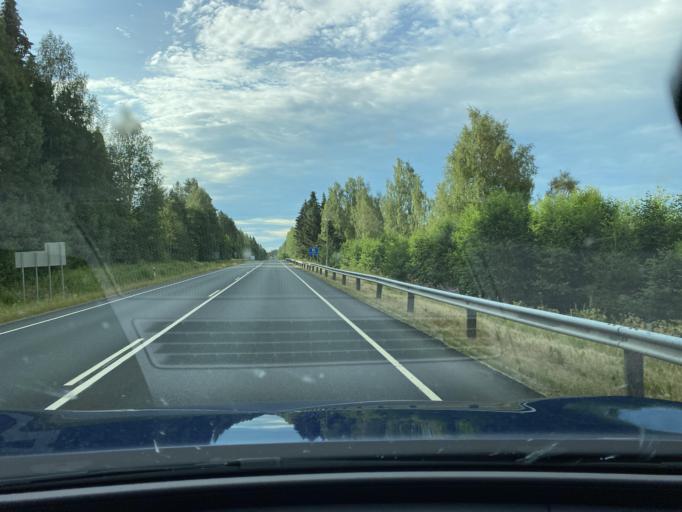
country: FI
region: Central Ostrobothnia
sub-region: Kaustinen
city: Veteli
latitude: 63.4195
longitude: 23.9374
